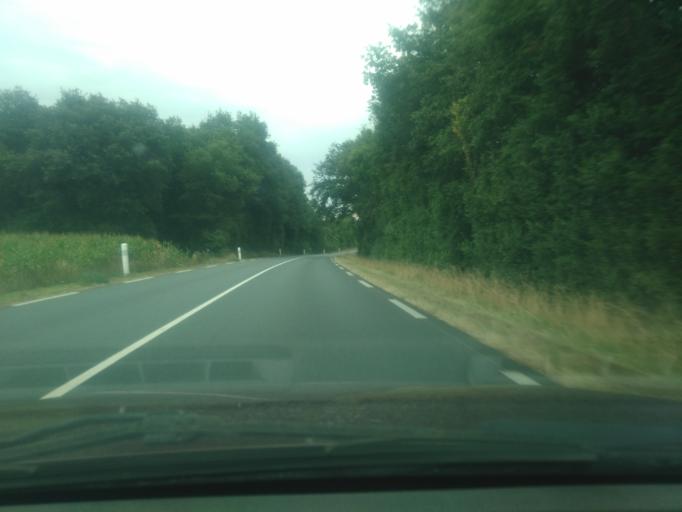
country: FR
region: Centre
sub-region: Departement de l'Indre
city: Belabre
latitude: 46.6355
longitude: 1.2676
